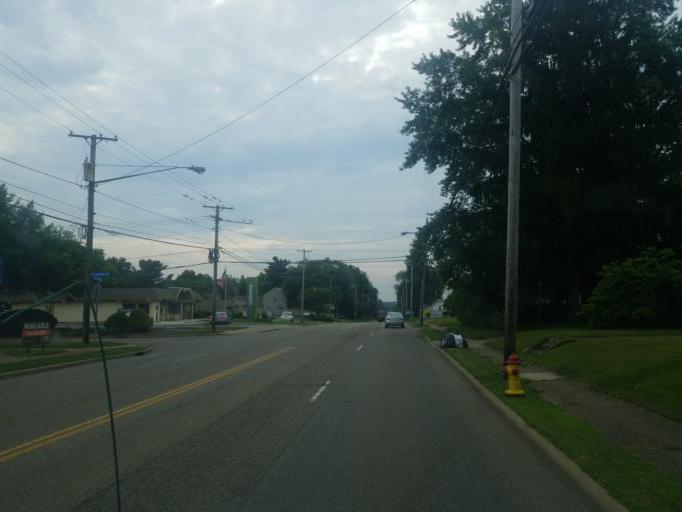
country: US
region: Ohio
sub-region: Stark County
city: Massillon
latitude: 40.7951
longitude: -81.5494
